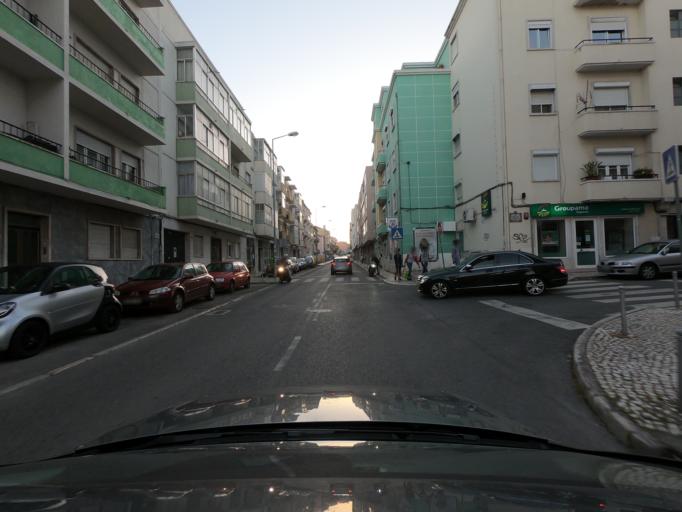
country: PT
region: Lisbon
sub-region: Sintra
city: Queluz
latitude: 38.7565
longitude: -9.2509
